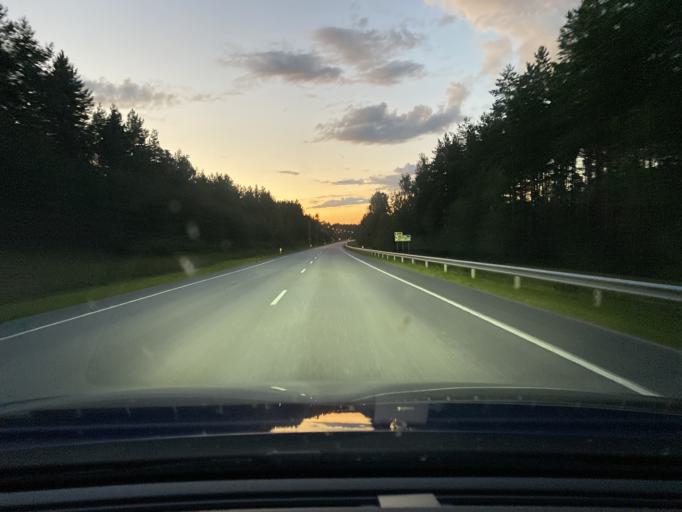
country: FI
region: Varsinais-Suomi
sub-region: Loimaa
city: Oripaeae
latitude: 60.9276
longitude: 22.6842
